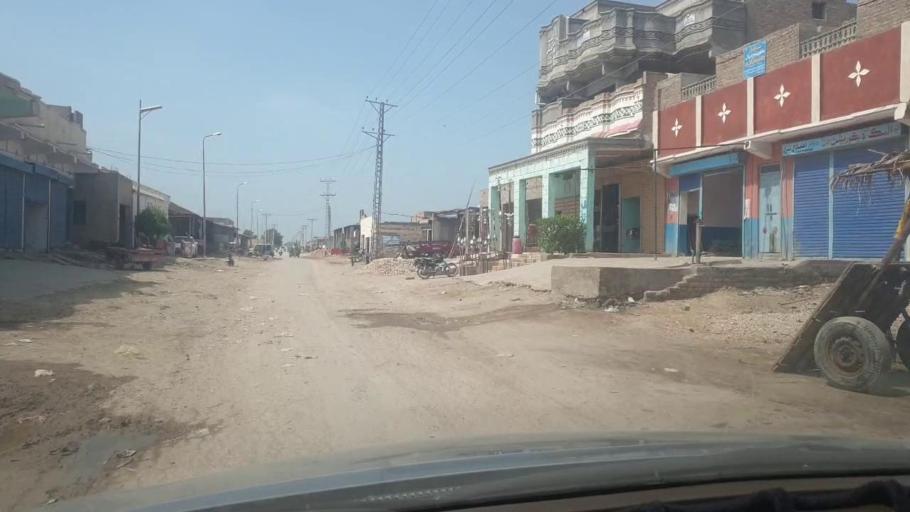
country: PK
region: Sindh
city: Gambat
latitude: 27.2983
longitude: 68.6101
